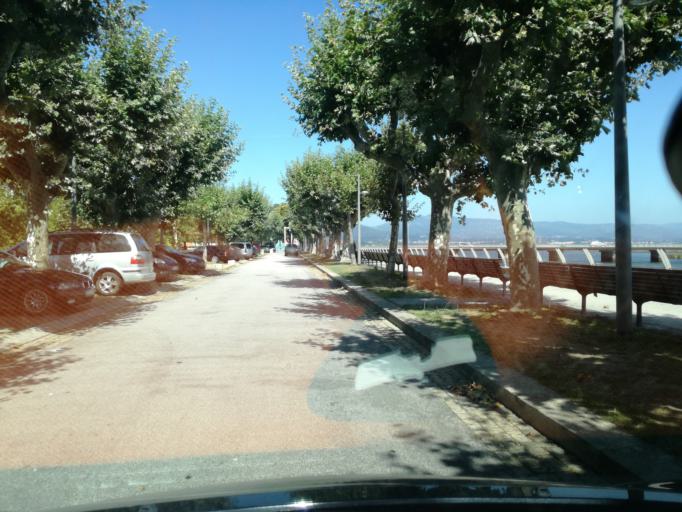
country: ES
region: Galicia
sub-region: Provincia de Pontevedra
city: A Guarda
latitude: 41.8768
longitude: -8.8342
